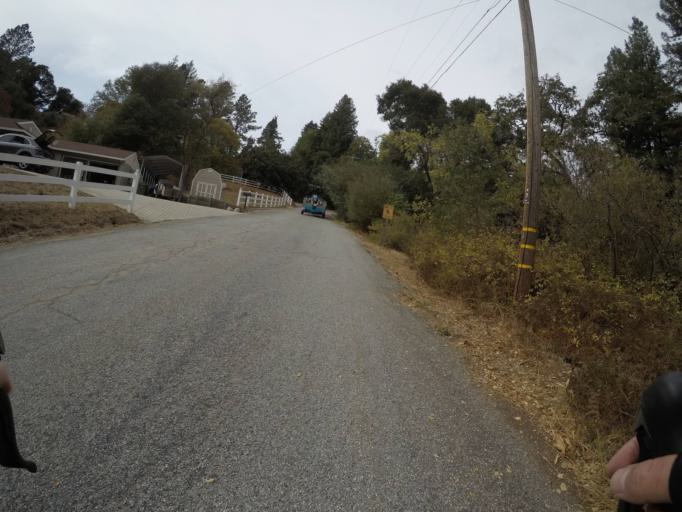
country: US
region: California
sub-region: Santa Cruz County
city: Mount Hermon
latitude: 37.0686
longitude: -122.0584
